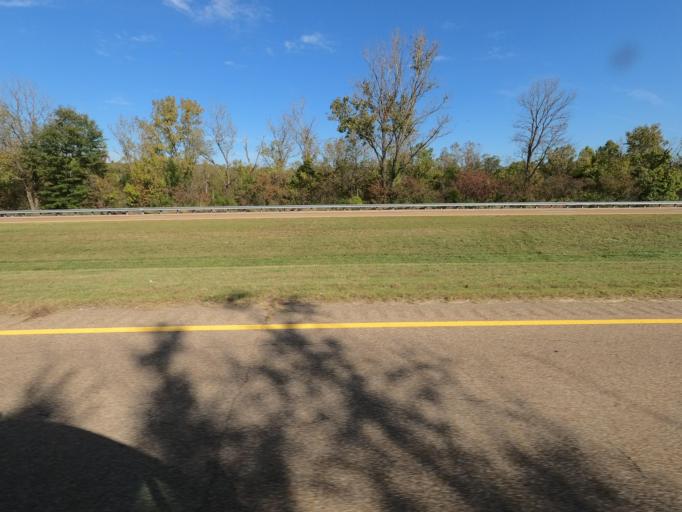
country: US
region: Tennessee
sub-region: Shelby County
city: Millington
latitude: 35.3303
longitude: -89.9058
